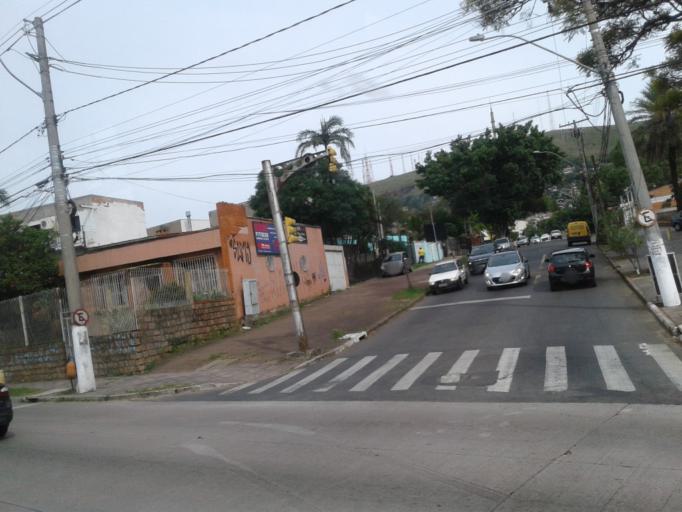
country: BR
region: Rio Grande do Sul
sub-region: Porto Alegre
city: Porto Alegre
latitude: -30.0722
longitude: -51.1931
